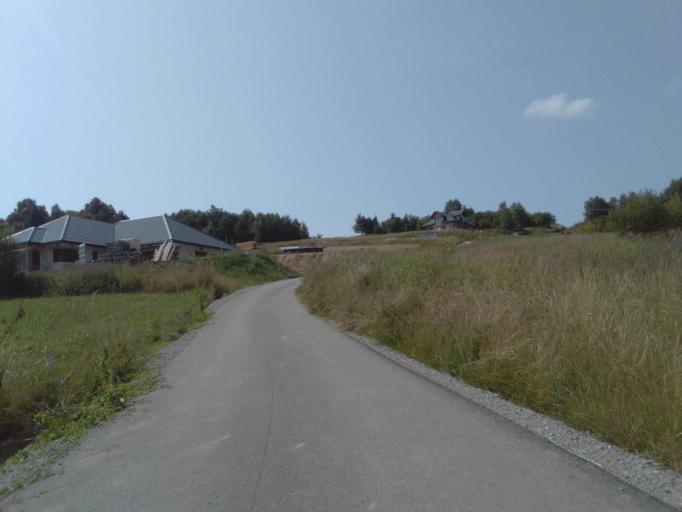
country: PL
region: Subcarpathian Voivodeship
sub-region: Powiat brzozowski
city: Domaradz
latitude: 49.7878
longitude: 21.9394
